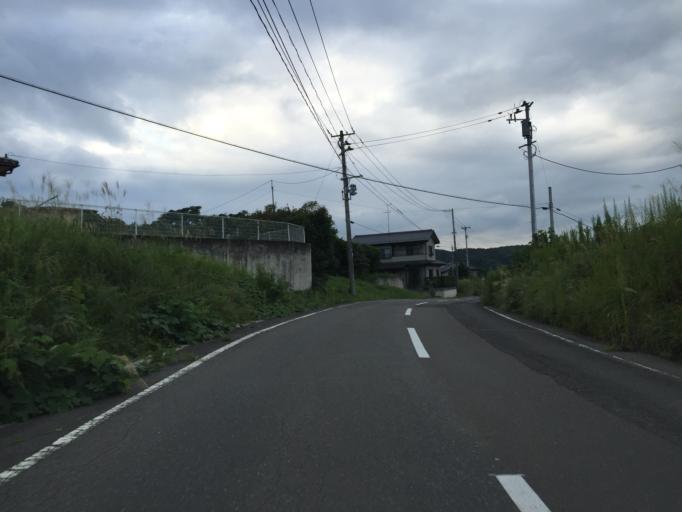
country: JP
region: Fukushima
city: Fukushima-shi
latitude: 37.6771
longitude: 140.4681
